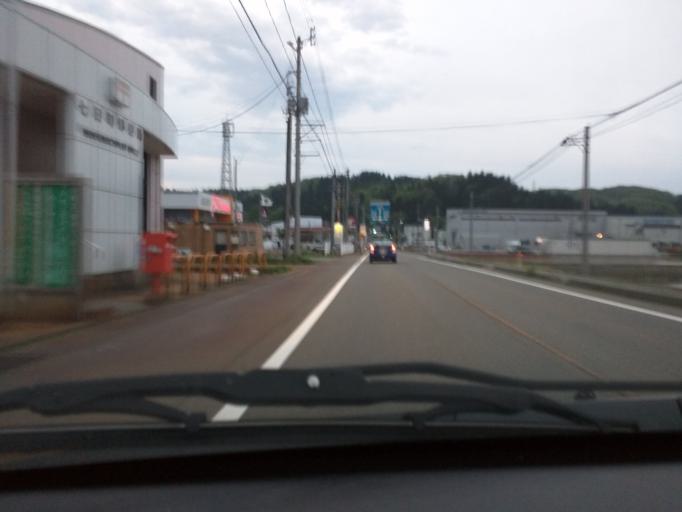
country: JP
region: Niigata
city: Ojiya
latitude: 37.3216
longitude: 138.7153
